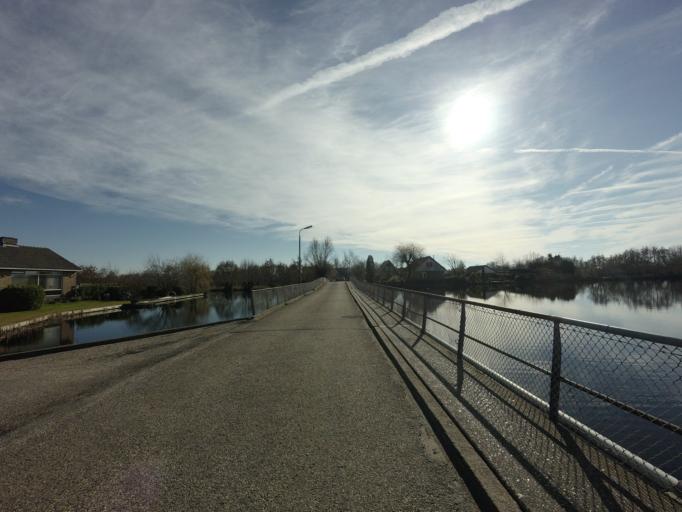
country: NL
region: South Holland
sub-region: Gemeente Kaag en Braassem
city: Oude Wetering
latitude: 52.2002
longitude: 4.6388
